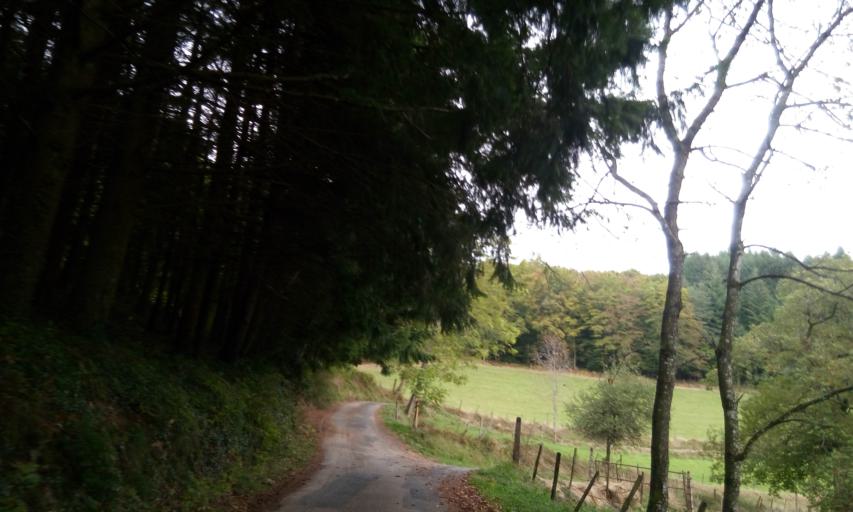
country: FR
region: Rhone-Alpes
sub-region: Departement du Rhone
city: Cours-la-Ville
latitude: 46.0843
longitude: 4.3648
